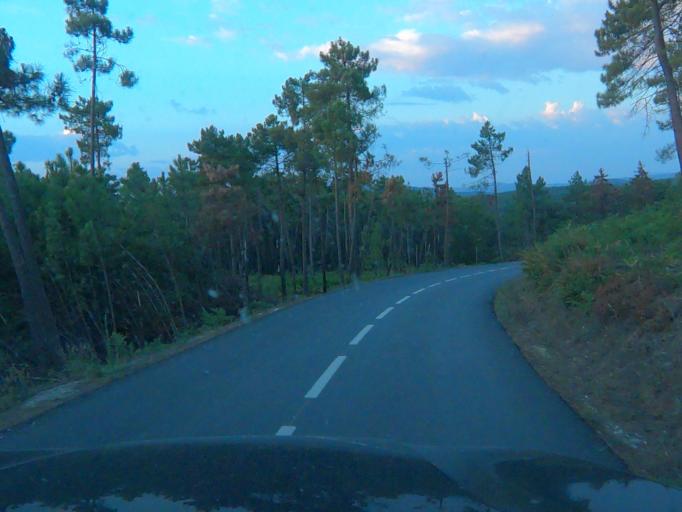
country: PT
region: Vila Real
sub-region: Sabrosa
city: Vilela
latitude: 41.2324
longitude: -7.6227
